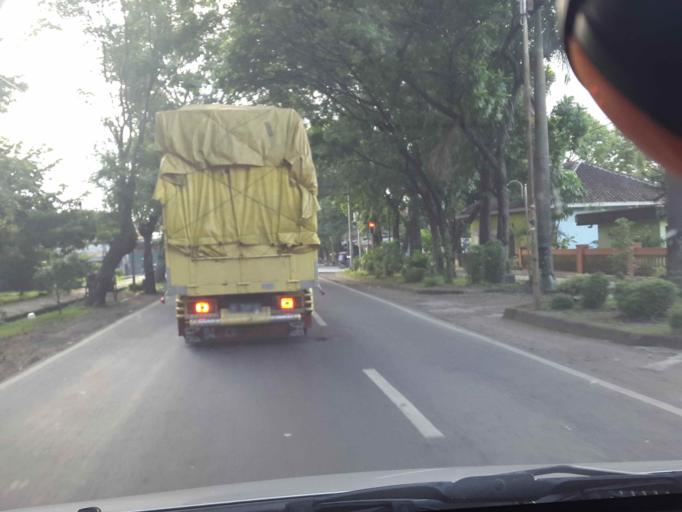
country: ID
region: Central Java
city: Sragen
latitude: -7.4317
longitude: 111.0249
